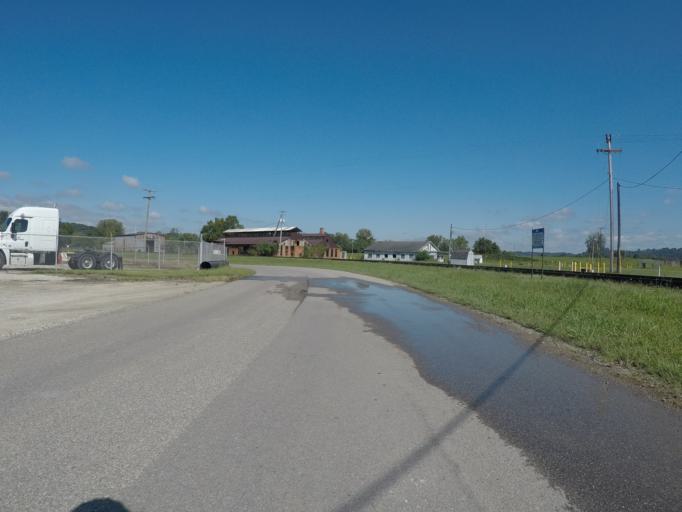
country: US
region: Ohio
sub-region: Lawrence County
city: South Point
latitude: 38.4075
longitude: -82.5892
